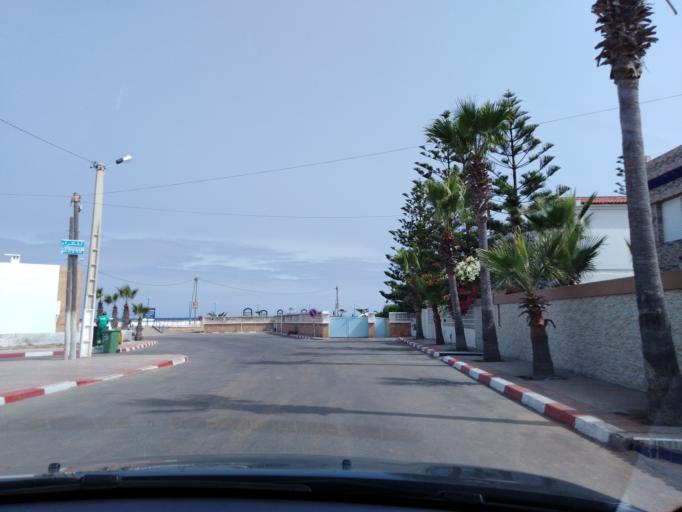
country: MA
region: Doukkala-Abda
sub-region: Safi
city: Safi
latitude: 32.7357
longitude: -9.0439
